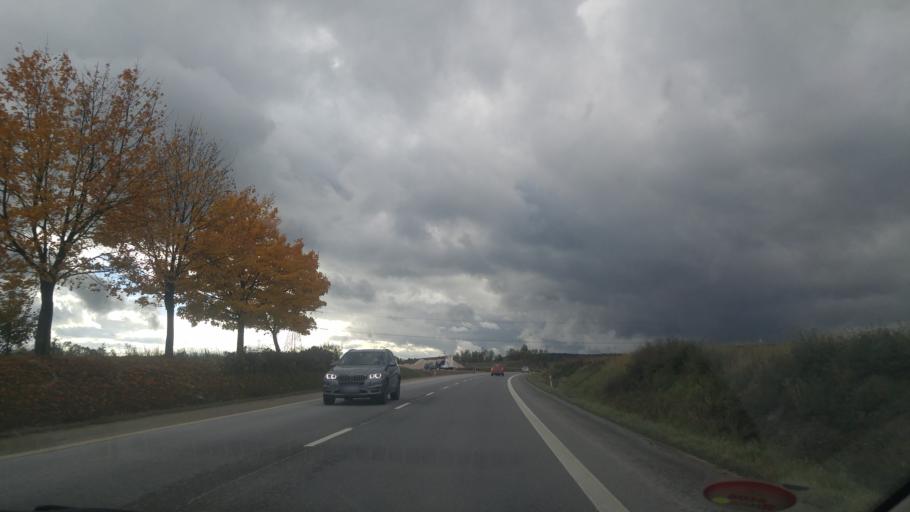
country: CZ
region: Jihocesky
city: Sevetin
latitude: 49.1157
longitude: 14.5857
